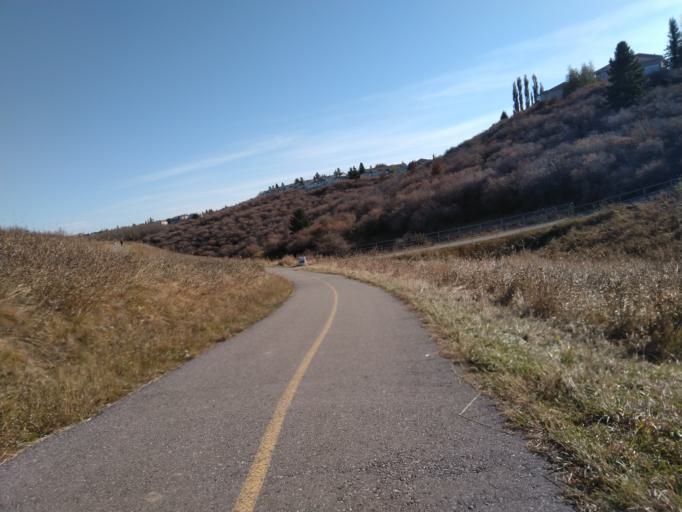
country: CA
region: Alberta
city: Calgary
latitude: 51.1368
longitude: -114.1481
